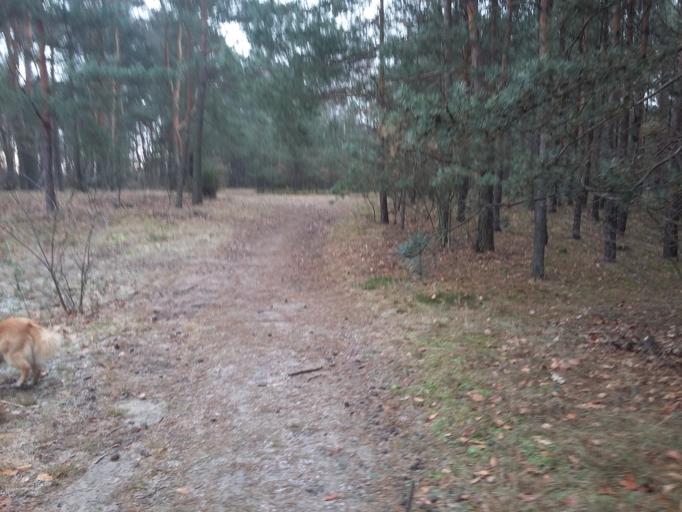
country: PL
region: Lodz Voivodeship
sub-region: Powiat pabianicki
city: Ksawerow
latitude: 51.7237
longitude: 19.3849
